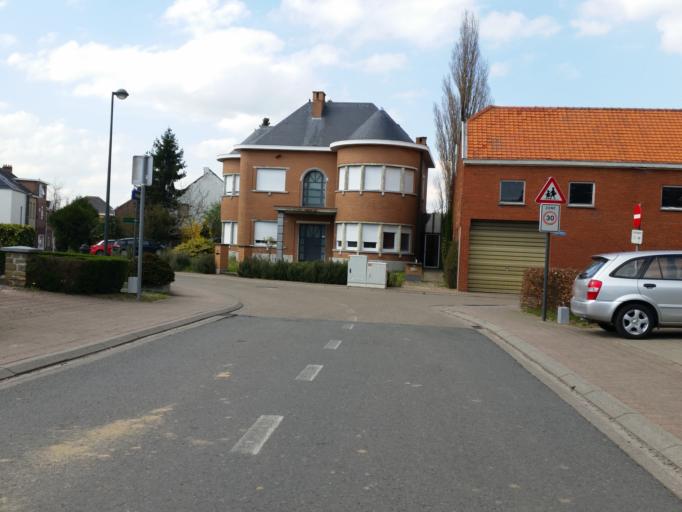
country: BE
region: Flanders
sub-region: Provincie Vlaams-Brabant
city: Kampenhout
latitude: 50.9198
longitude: 4.5622
